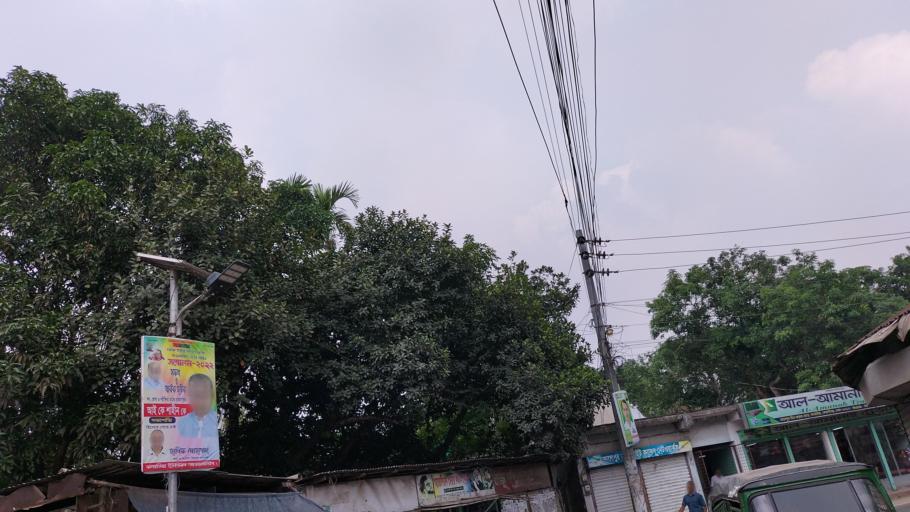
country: BD
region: Dhaka
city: Azimpur
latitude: 23.7009
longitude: 90.2940
